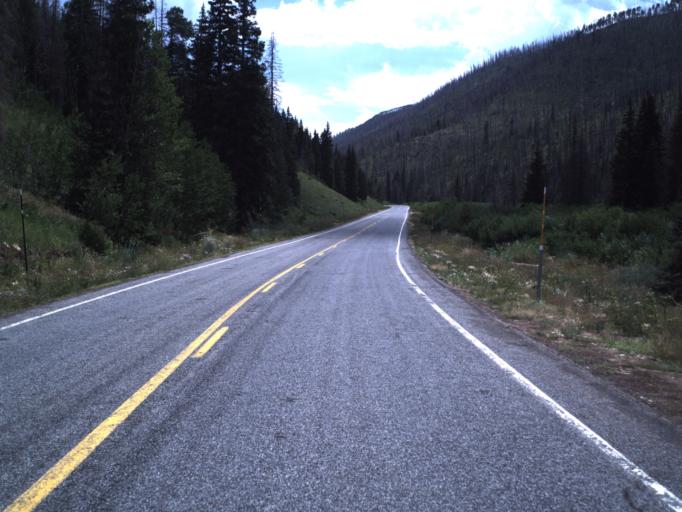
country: US
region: Utah
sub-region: Sanpete County
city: Fairview
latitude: 39.5605
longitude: -111.1751
